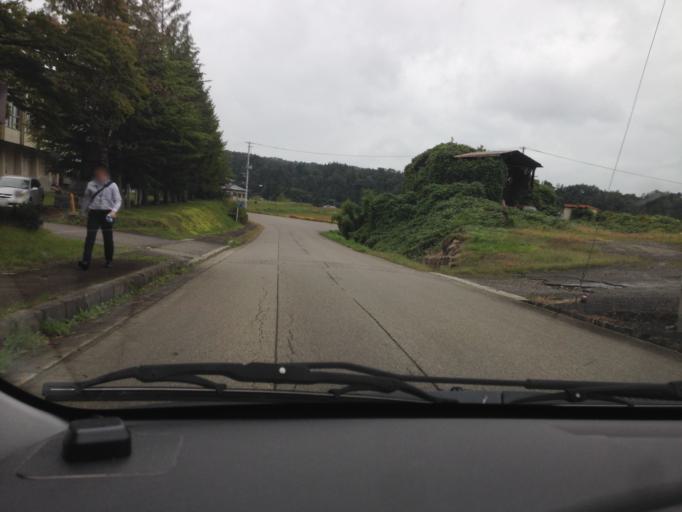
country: JP
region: Fukushima
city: Kitakata
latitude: 37.5074
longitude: 139.8123
